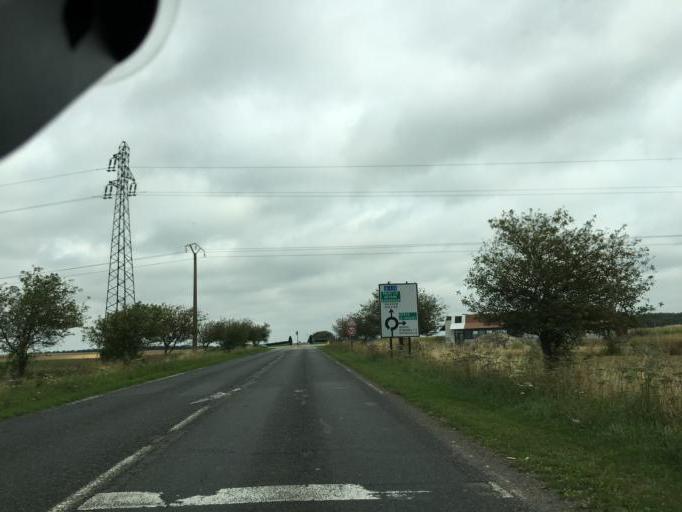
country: FR
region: Nord-Pas-de-Calais
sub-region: Departement du Pas-de-Calais
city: Saint-Pol-sur-Ternoise
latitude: 50.3893
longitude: 2.3512
